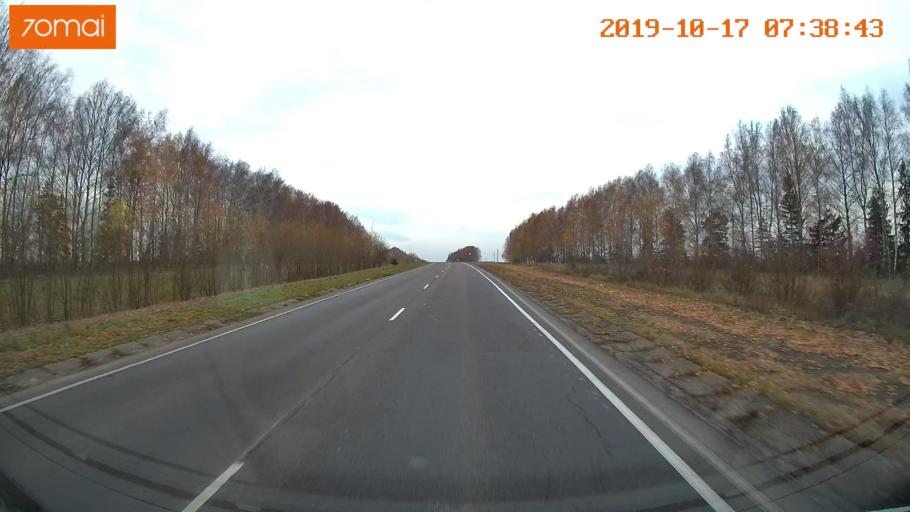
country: RU
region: Vladimir
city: Yur'yev-Pol'skiy
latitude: 56.4576
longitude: 39.8673
